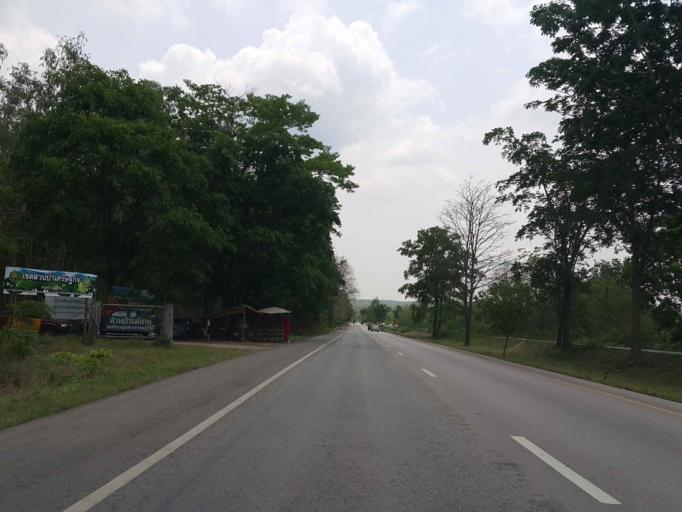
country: TH
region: Lampang
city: Ko Kha
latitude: 18.0767
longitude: 99.3933
